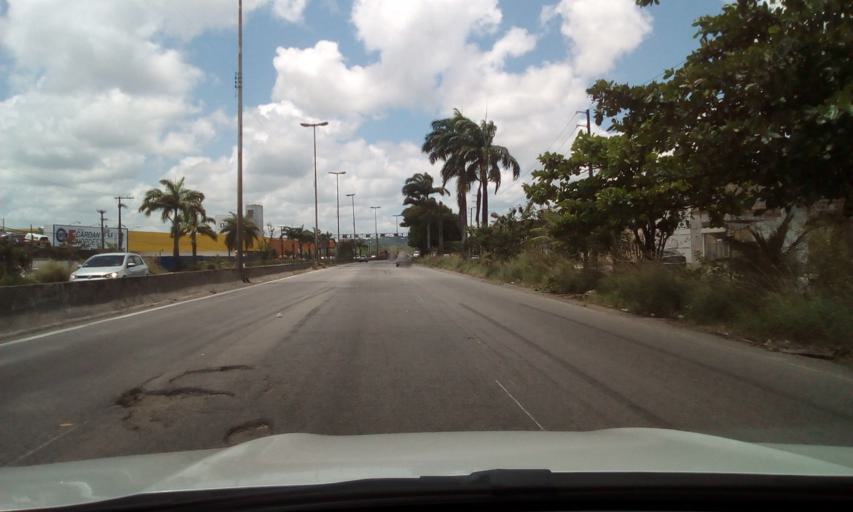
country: BR
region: Pernambuco
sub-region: Recife
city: Recife
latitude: -8.0319
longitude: -34.9424
